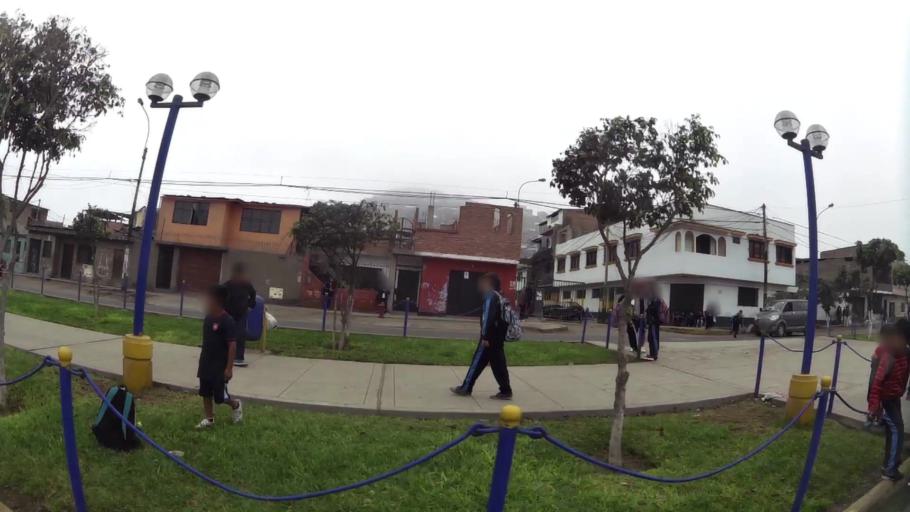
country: PE
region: Lima
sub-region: Lima
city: Surco
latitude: -12.1548
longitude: -76.9547
